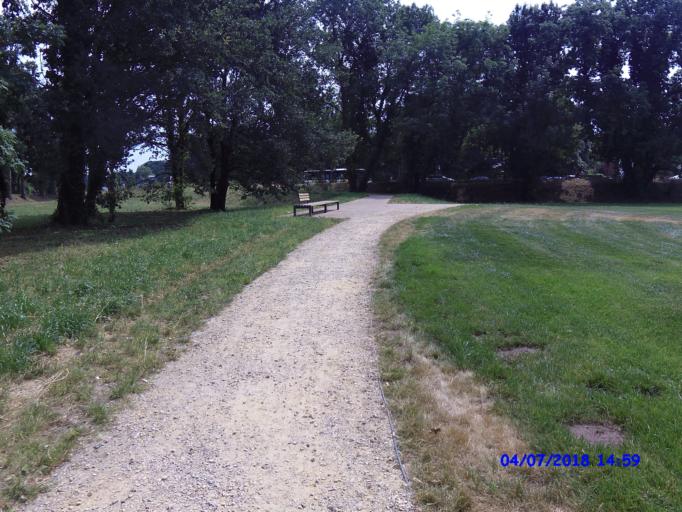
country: BE
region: Flanders
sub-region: Provincie Antwerpen
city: Herentals
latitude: 51.1804
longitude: 4.8390
